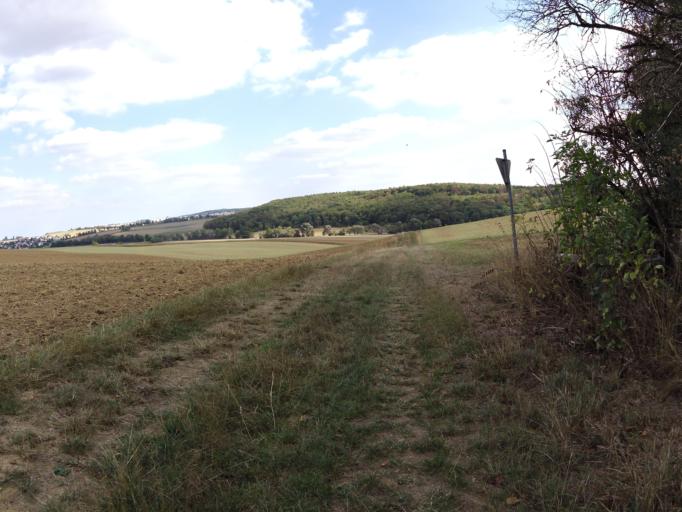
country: DE
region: Bavaria
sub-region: Regierungsbezirk Unterfranken
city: Hettstadt
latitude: 49.7947
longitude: 9.7994
